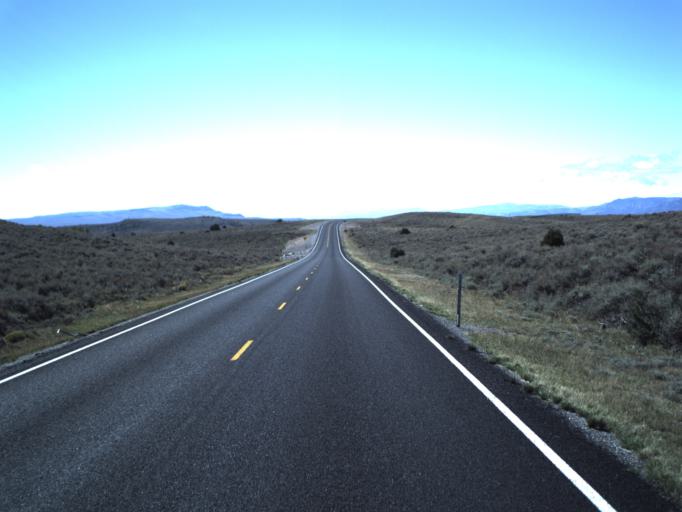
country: US
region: Utah
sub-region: Wayne County
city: Loa
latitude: 38.5048
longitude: -111.7966
